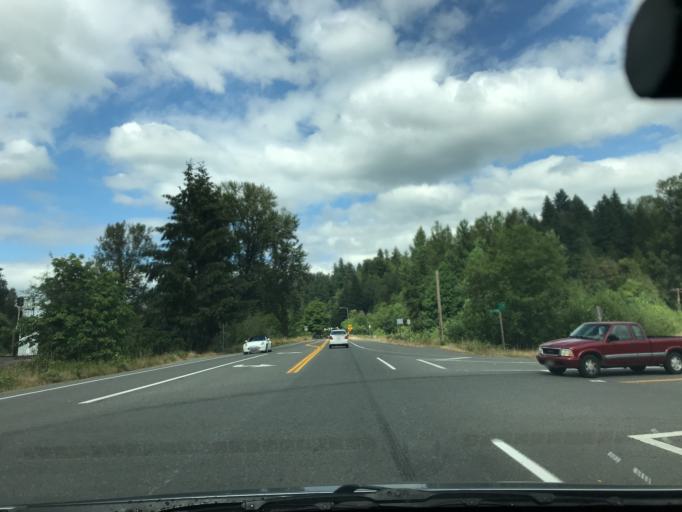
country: US
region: Washington
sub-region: King County
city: Lea Hill
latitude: 47.3009
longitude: -122.1776
